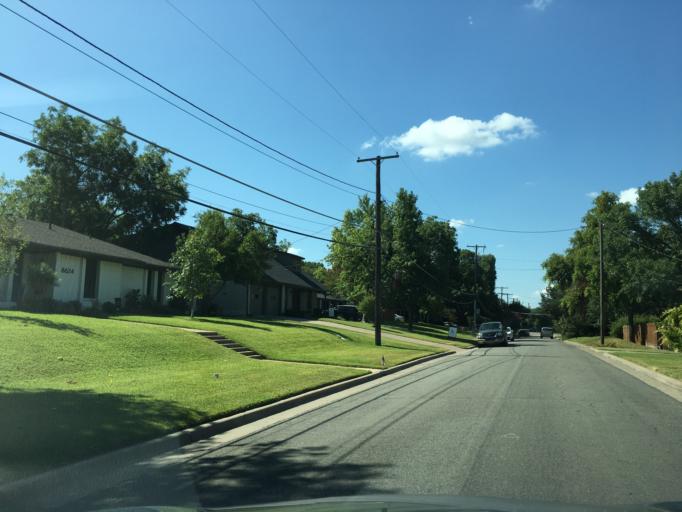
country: US
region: Texas
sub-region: Dallas County
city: Garland
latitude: 32.8666
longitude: -96.6978
